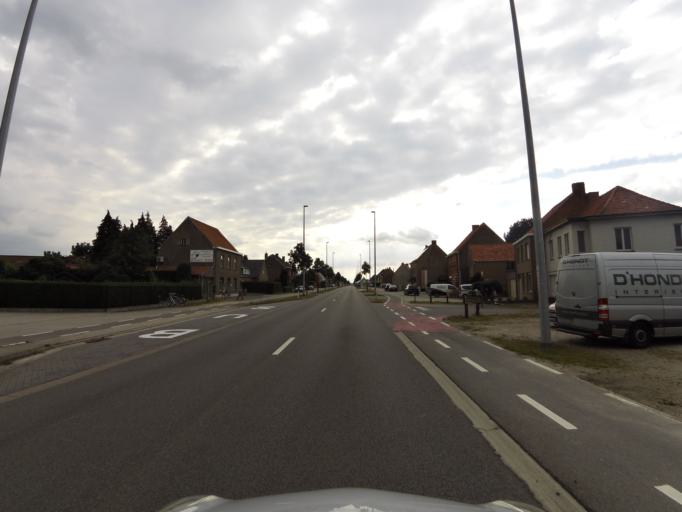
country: BE
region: Flanders
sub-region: Provincie Oost-Vlaanderen
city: Deinze
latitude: 50.9608
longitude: 3.5022
